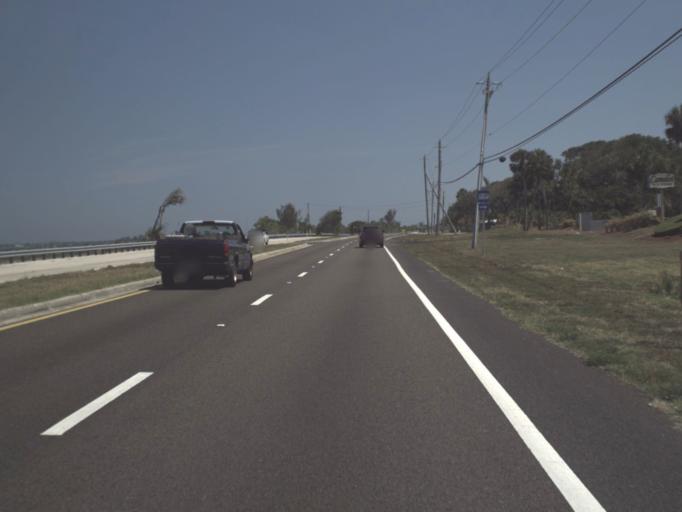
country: US
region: Florida
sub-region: Brevard County
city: Malabar
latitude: 28.0009
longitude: -80.5614
